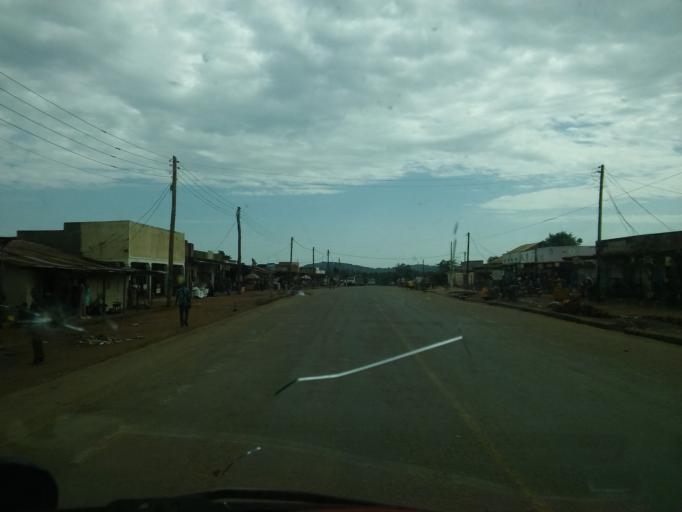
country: UG
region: Eastern Region
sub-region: Mbale District
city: Mbale
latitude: 1.1434
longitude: 34.1645
